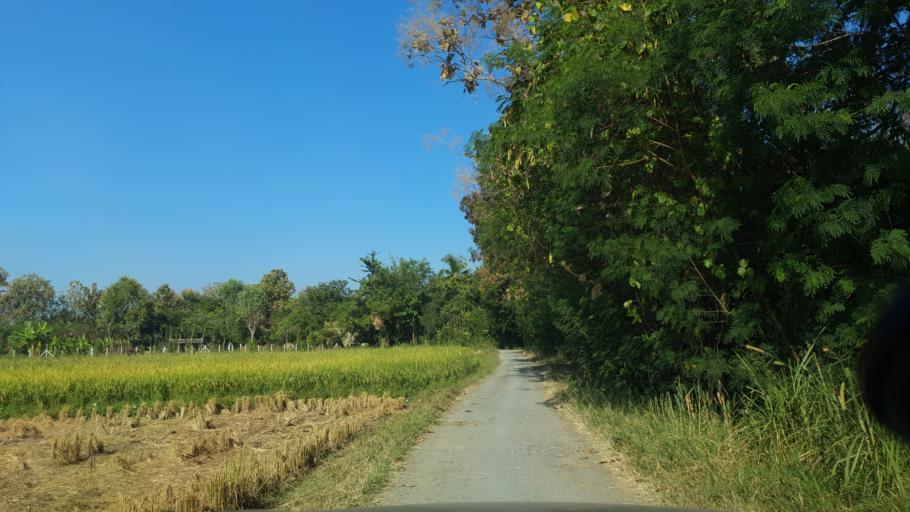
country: TH
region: Chiang Mai
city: San Kamphaeng
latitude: 18.7350
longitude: 99.1675
